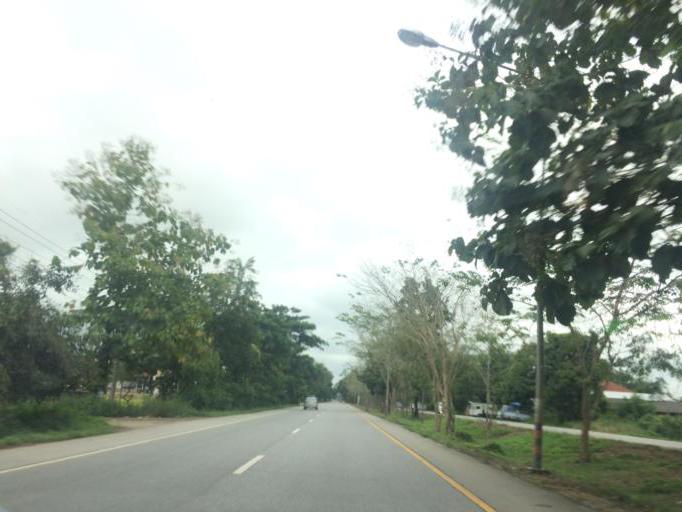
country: TH
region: Chiang Rai
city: Mae Lao
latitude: 19.8097
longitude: 99.7561
